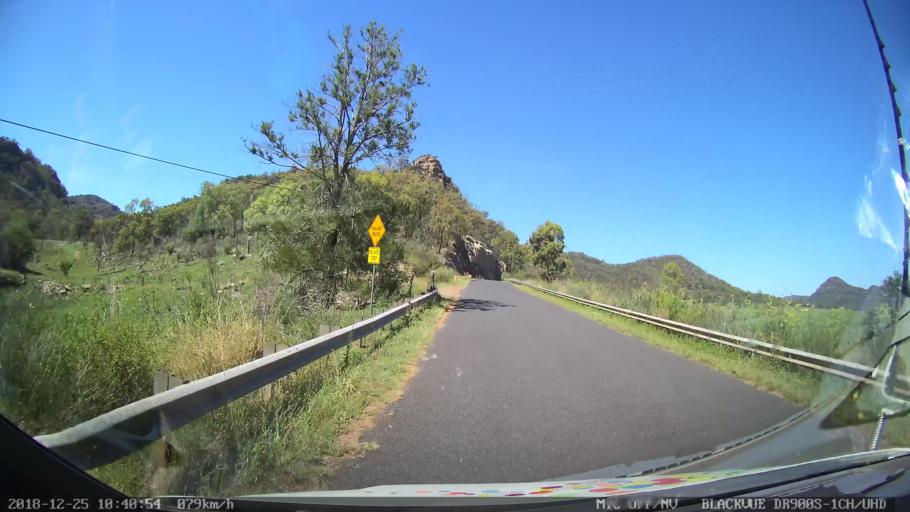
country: AU
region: New South Wales
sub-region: Upper Hunter Shire
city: Merriwa
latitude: -32.4123
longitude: 150.3400
